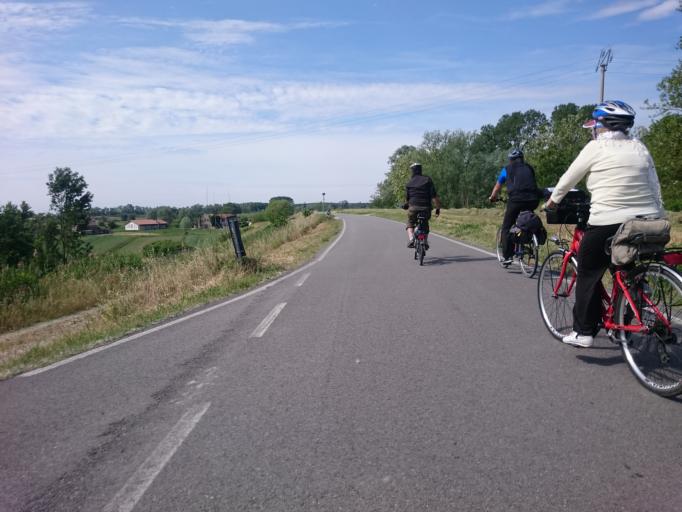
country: IT
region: Veneto
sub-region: Provincia di Rovigo
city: Corbola
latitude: 44.9805
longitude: 12.0842
